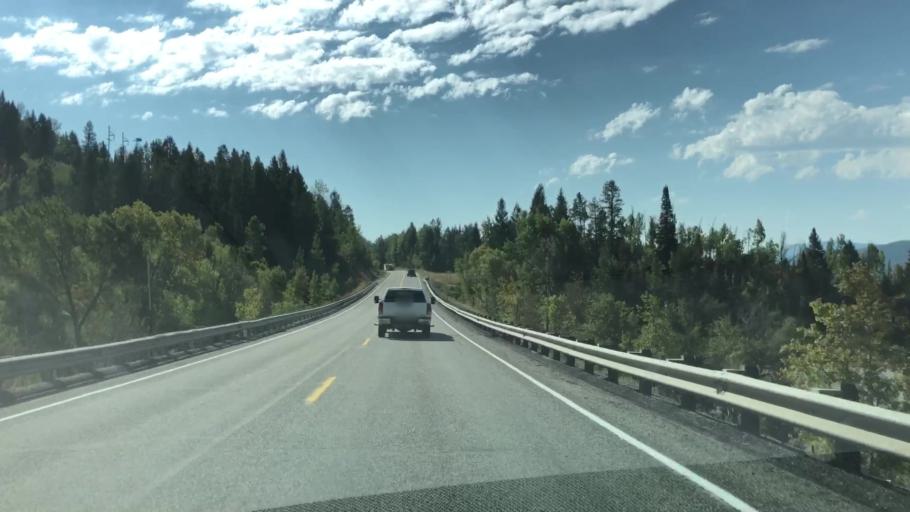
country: US
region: Idaho
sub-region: Teton County
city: Victor
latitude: 43.2838
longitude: -111.1198
